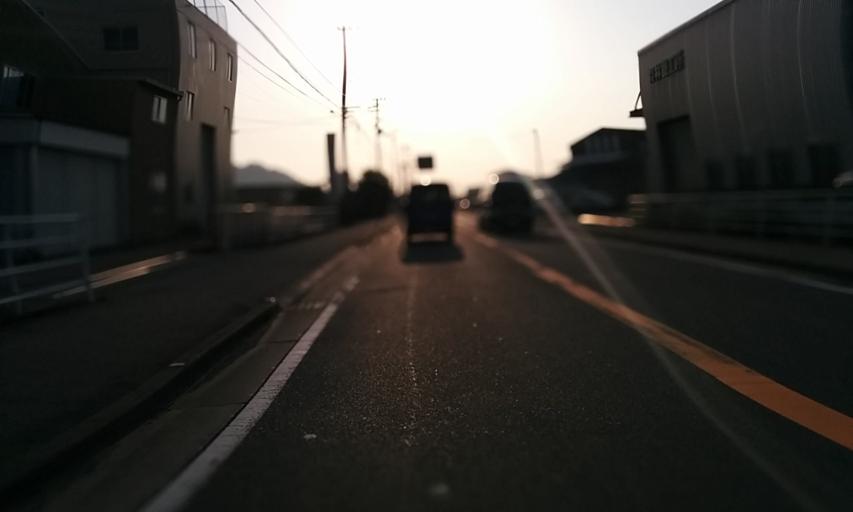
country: JP
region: Ehime
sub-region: Shikoku-chuo Shi
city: Matsuyama
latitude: 33.7823
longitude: 132.8067
